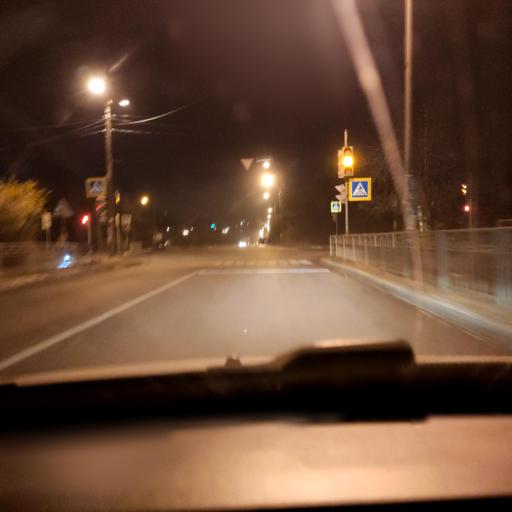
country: RU
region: Voronezj
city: Voronezh
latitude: 51.6973
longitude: 39.1568
